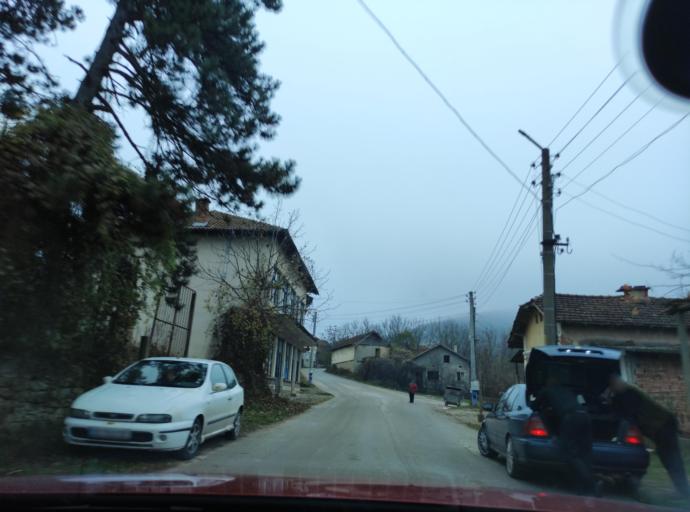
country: BG
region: Lovech
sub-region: Obshtina Yablanitsa
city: Yablanitsa
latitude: 43.1183
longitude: 24.0635
